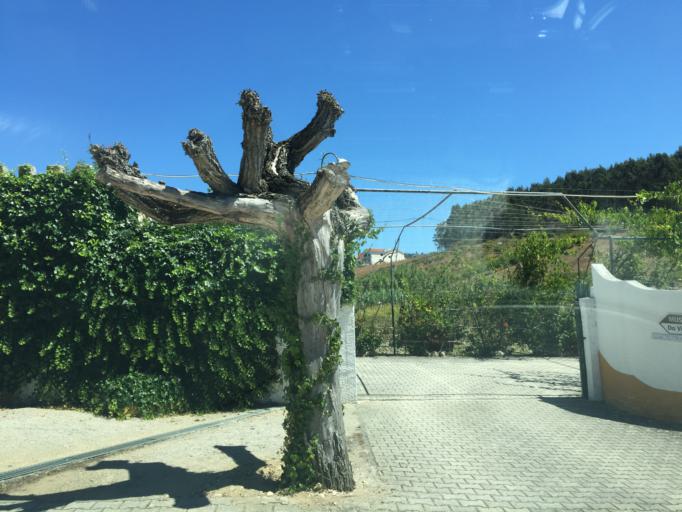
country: PT
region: Lisbon
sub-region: Torres Vedras
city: A dos Cunhados
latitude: 39.1882
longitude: -9.3023
